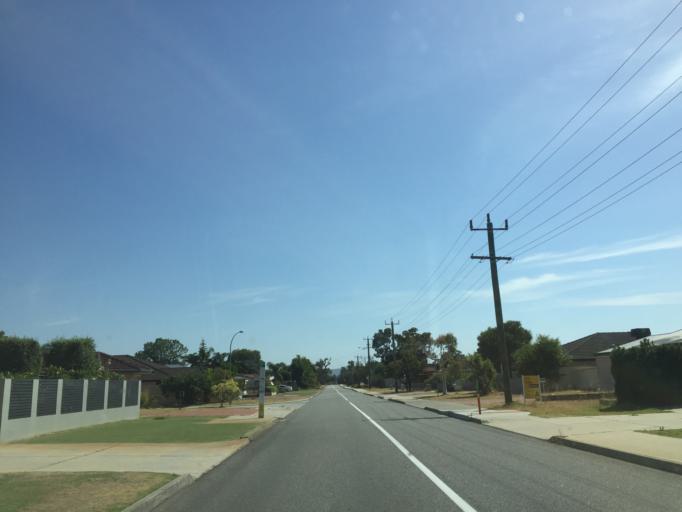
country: AU
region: Western Australia
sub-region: Gosnells
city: Southern River
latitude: -32.0845
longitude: 115.9576
